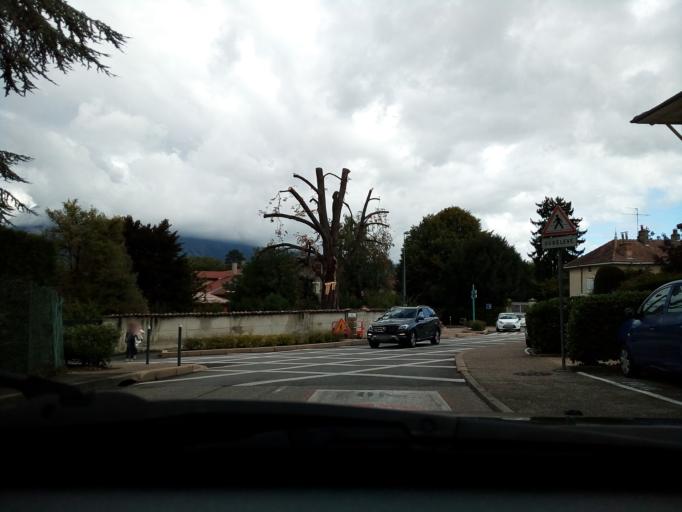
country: FR
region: Rhone-Alpes
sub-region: Departement de l'Isere
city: Gieres
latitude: 45.1825
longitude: 5.7882
